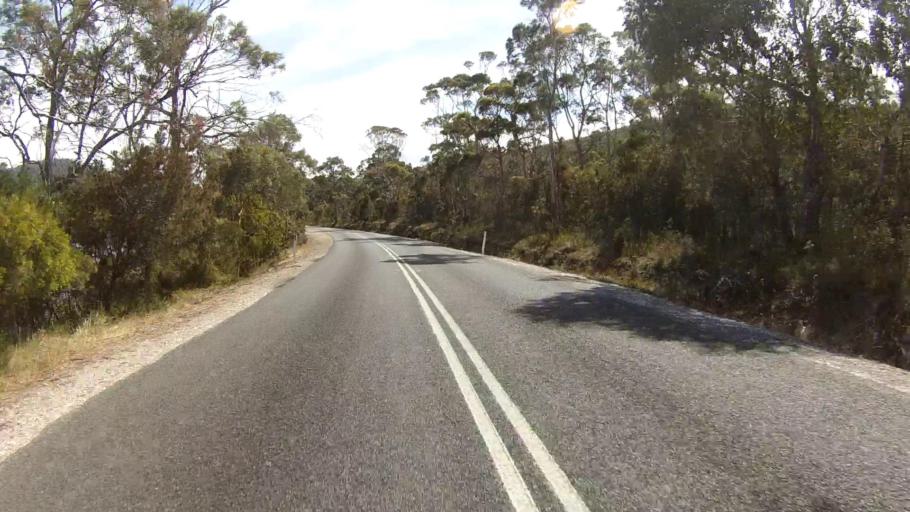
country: AU
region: Tasmania
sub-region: Huon Valley
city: Cygnet
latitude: -43.2627
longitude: 147.1435
